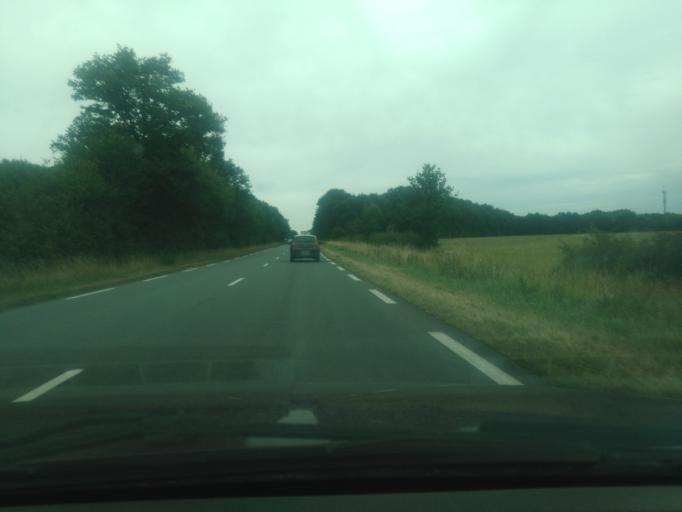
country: FR
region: Poitou-Charentes
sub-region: Departement de la Vienne
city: Chauvigny
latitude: 46.5726
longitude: 0.7395
